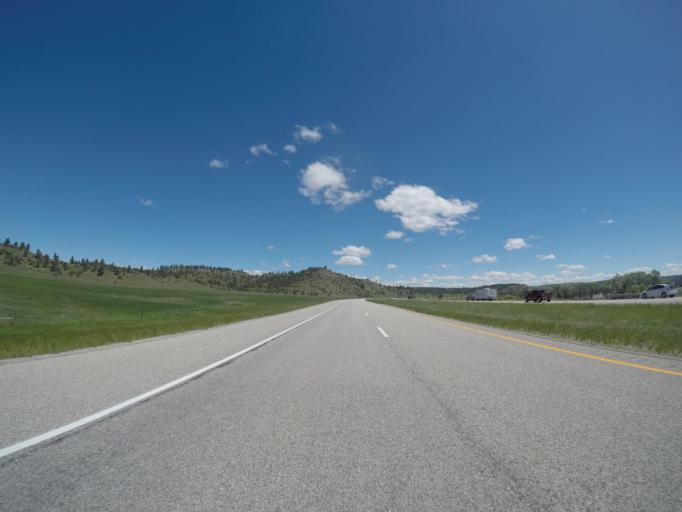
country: US
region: Montana
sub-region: Stillwater County
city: Columbus
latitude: 45.6935
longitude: -109.4130
